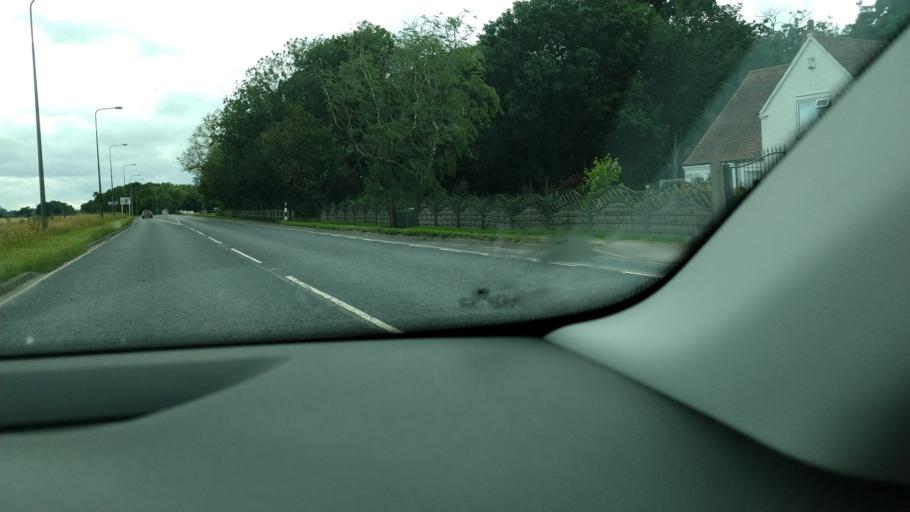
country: GB
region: England
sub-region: East Riding of Yorkshire
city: Rawcliffe
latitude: 53.7068
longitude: -0.9297
